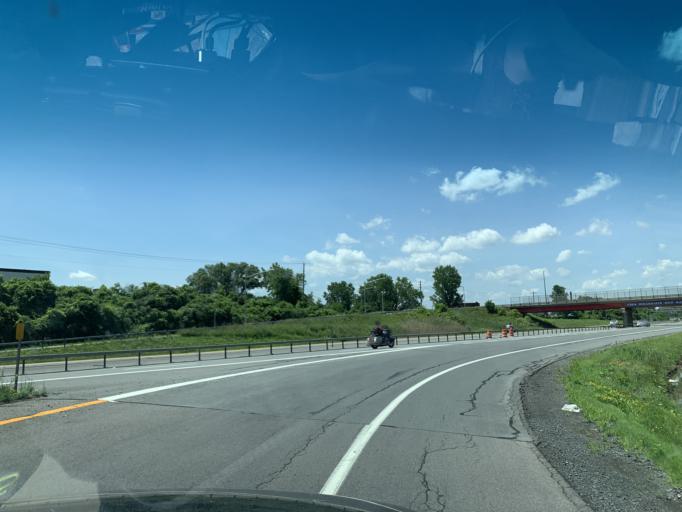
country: US
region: New York
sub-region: Oneida County
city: Utica
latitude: 43.0958
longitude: -75.1909
